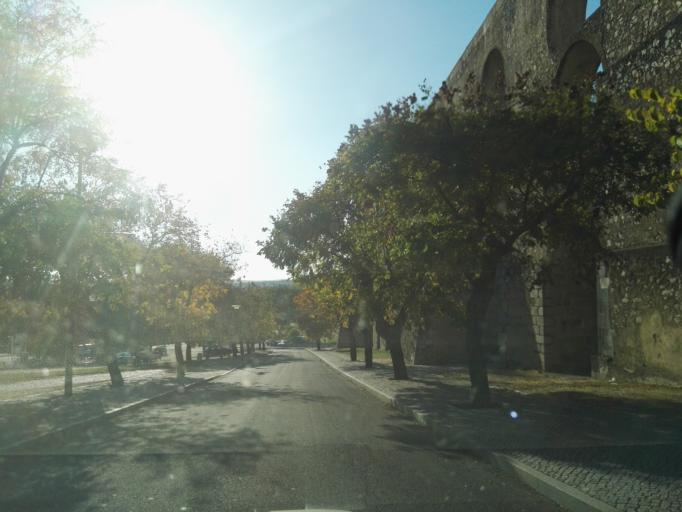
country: PT
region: Portalegre
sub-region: Elvas
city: Elvas
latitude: 38.8784
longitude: -7.1704
